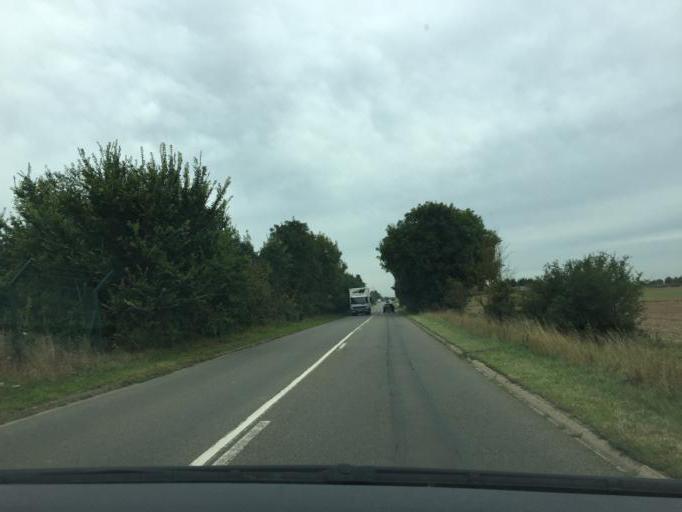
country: FR
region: Ile-de-France
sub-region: Departement des Yvelines
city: Les Loges-en-Josas
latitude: 48.7561
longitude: 2.1213
